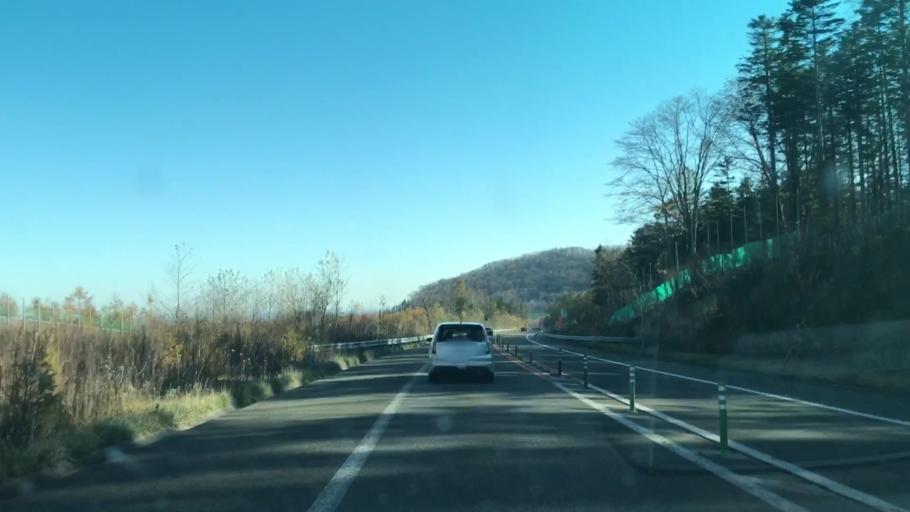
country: JP
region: Hokkaido
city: Otofuke
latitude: 43.0155
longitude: 142.8300
